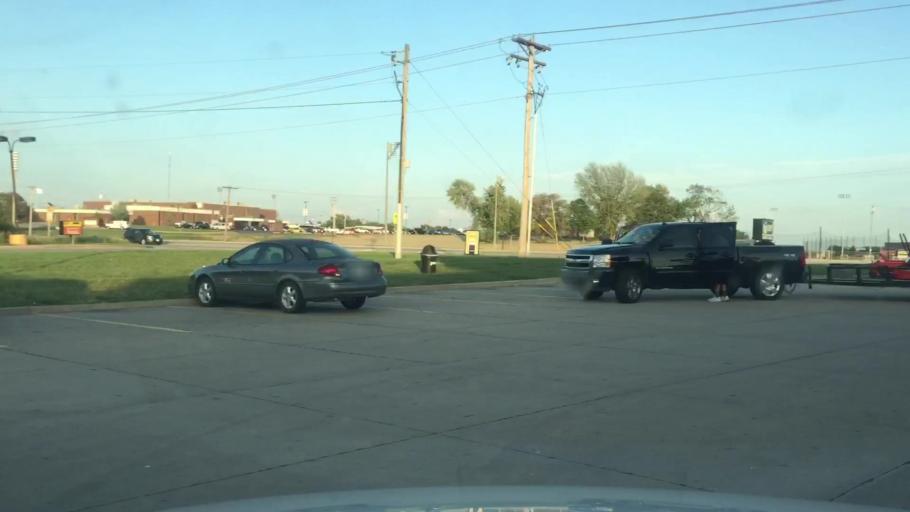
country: US
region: Missouri
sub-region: Cooper County
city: Boonville
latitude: 38.9395
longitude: -92.7737
